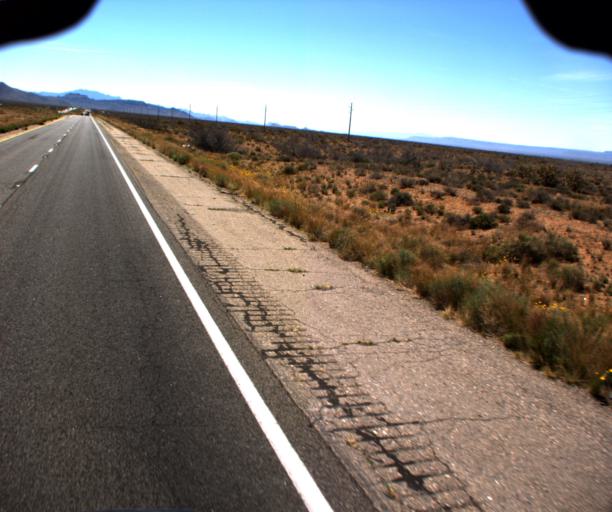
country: US
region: Arizona
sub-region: Mohave County
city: Golden Valley
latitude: 35.3122
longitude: -114.1983
